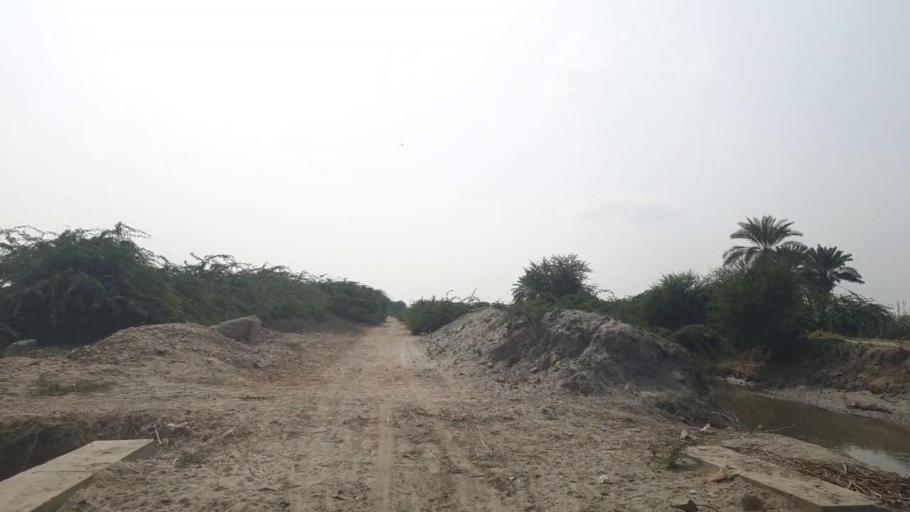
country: PK
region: Sindh
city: Badin
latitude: 24.6026
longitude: 68.7191
